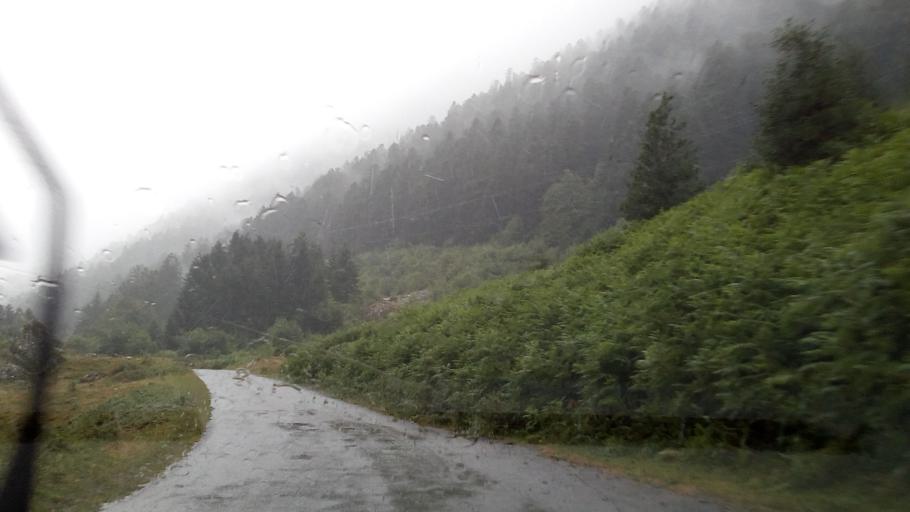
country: FR
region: Midi-Pyrenees
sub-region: Departement des Hautes-Pyrenees
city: Cauterets
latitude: 42.9039
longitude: -0.2614
